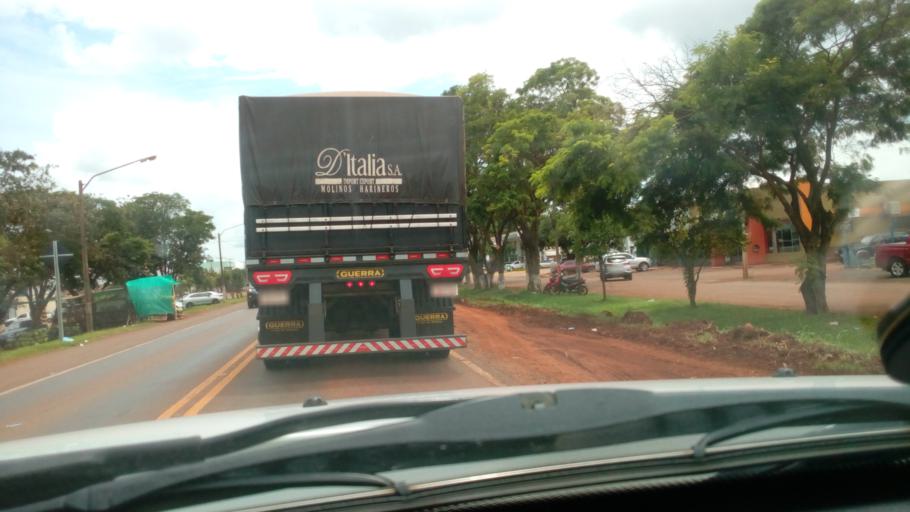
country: PY
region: Alto Parana
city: Santa Rita
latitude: -25.7811
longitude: -55.0781
